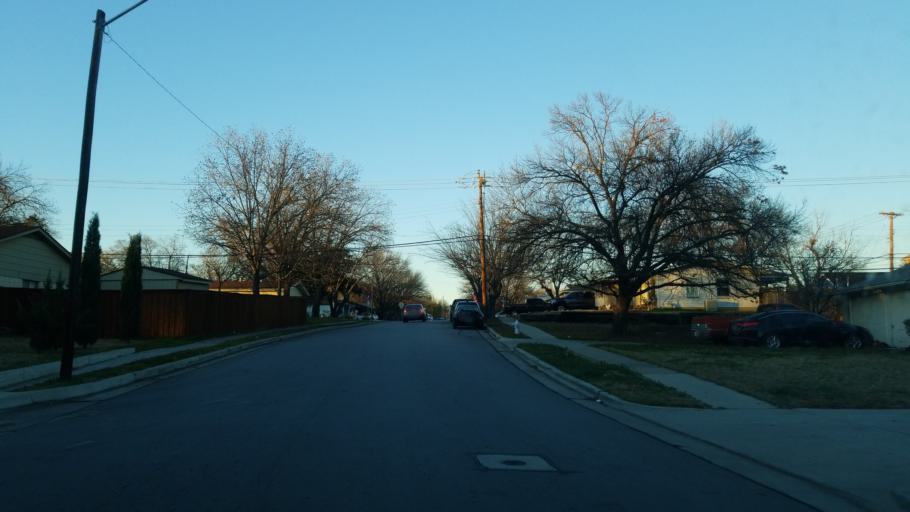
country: US
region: Texas
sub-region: Tarrant County
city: Arlington
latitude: 32.7275
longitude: -97.0572
